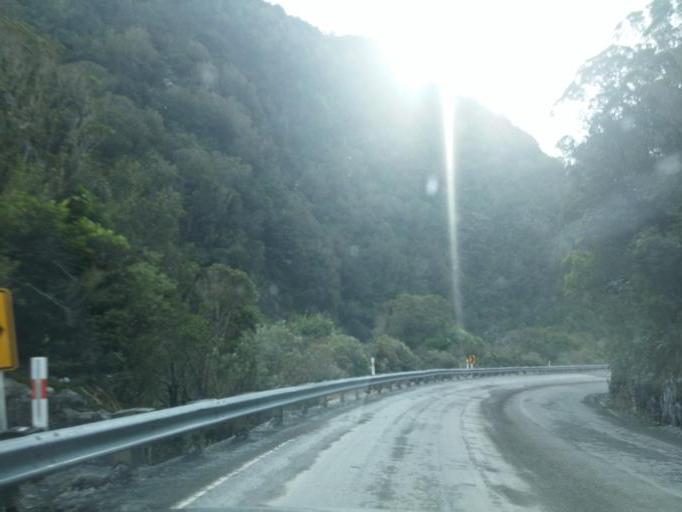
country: NZ
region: West Coast
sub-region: Grey District
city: Greymouth
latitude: -42.8824
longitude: 171.5549
